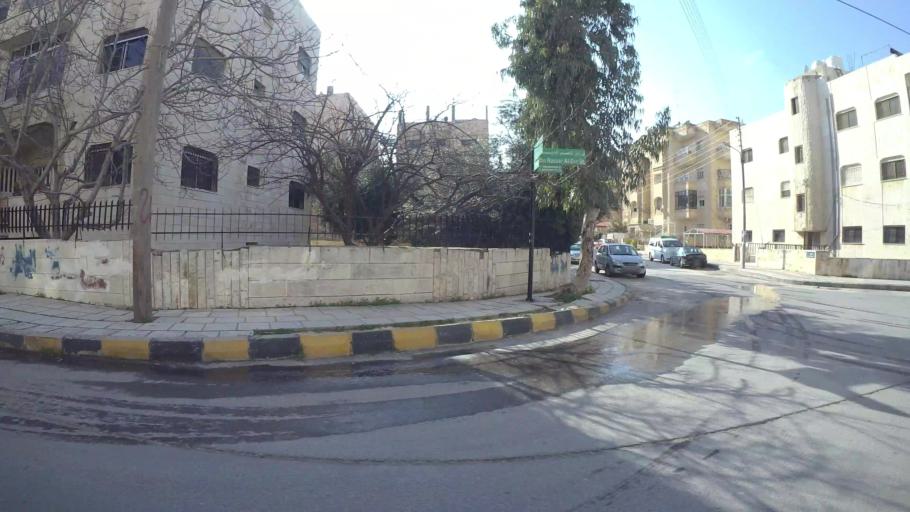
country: JO
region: Amman
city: Al Jubayhah
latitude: 32.0218
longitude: 35.8513
